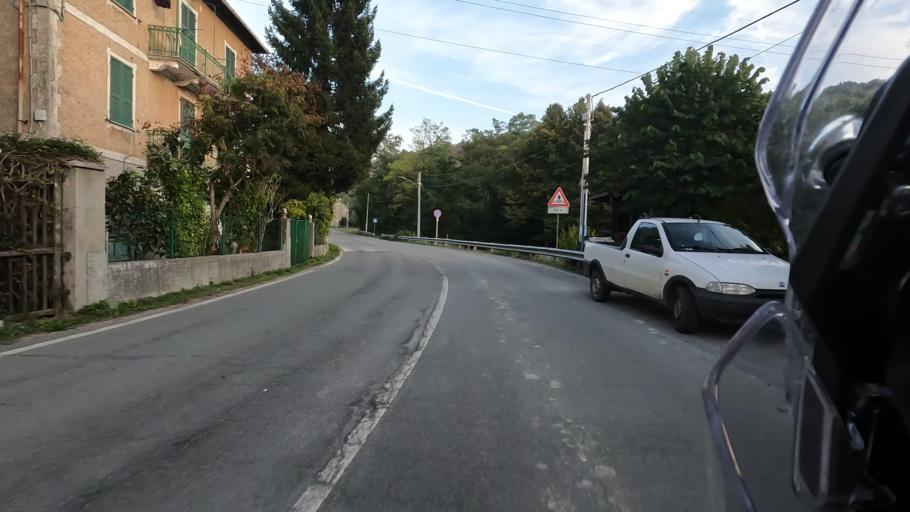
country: IT
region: Liguria
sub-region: Provincia di Savona
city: Osteria dei Cacciatori-Stella
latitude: 44.4302
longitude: 8.4589
